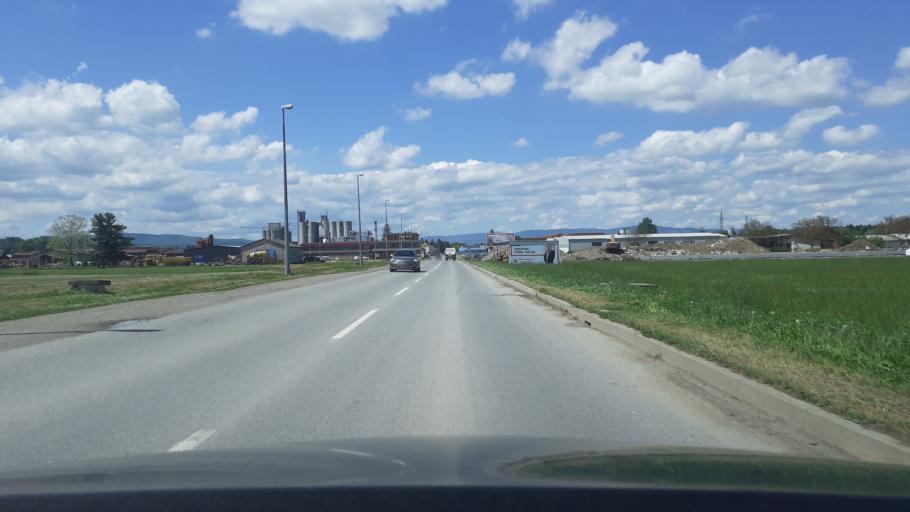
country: HR
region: Pozesko-Slavonska
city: Pozega
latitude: 45.3384
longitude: 17.7000
